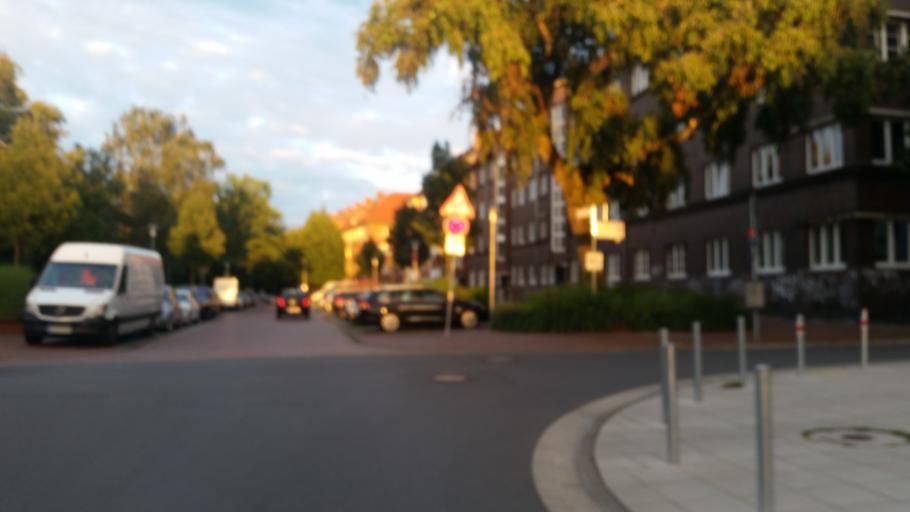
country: DE
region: Lower Saxony
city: Hannover
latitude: 52.4004
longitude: 9.7737
